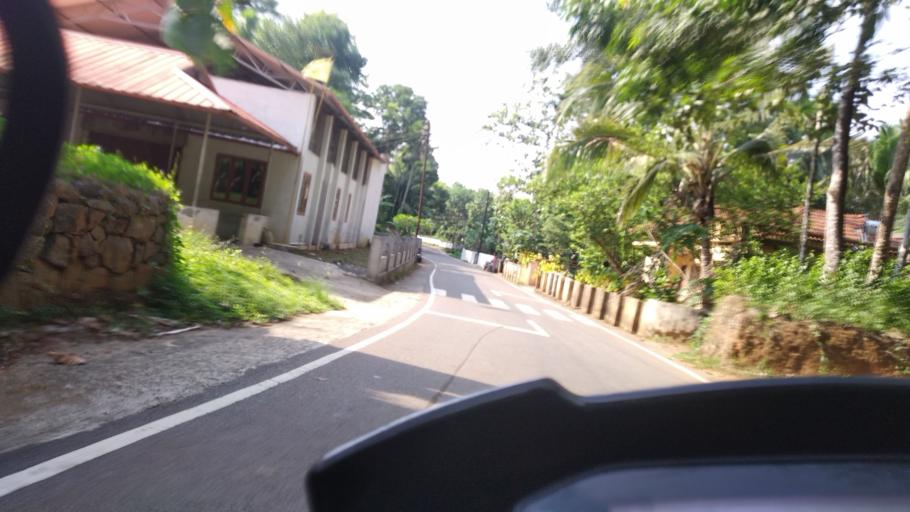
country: IN
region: Kerala
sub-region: Ernakulam
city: Piravam
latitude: 9.8358
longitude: 76.5394
